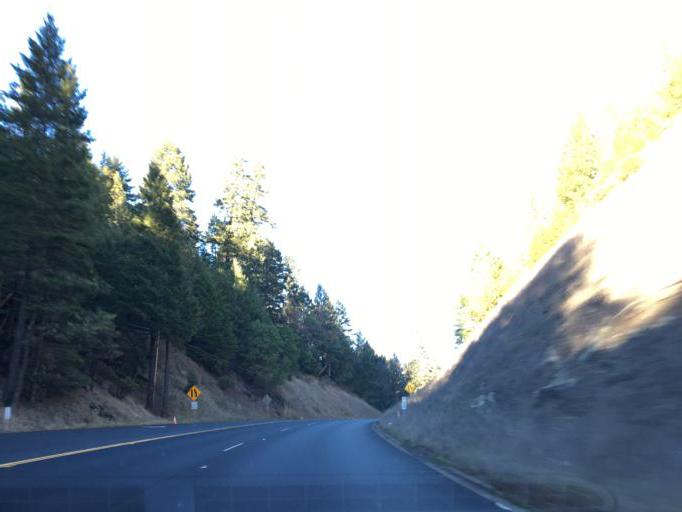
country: US
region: California
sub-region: Mendocino County
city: Laytonville
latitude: 39.7857
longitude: -123.5445
